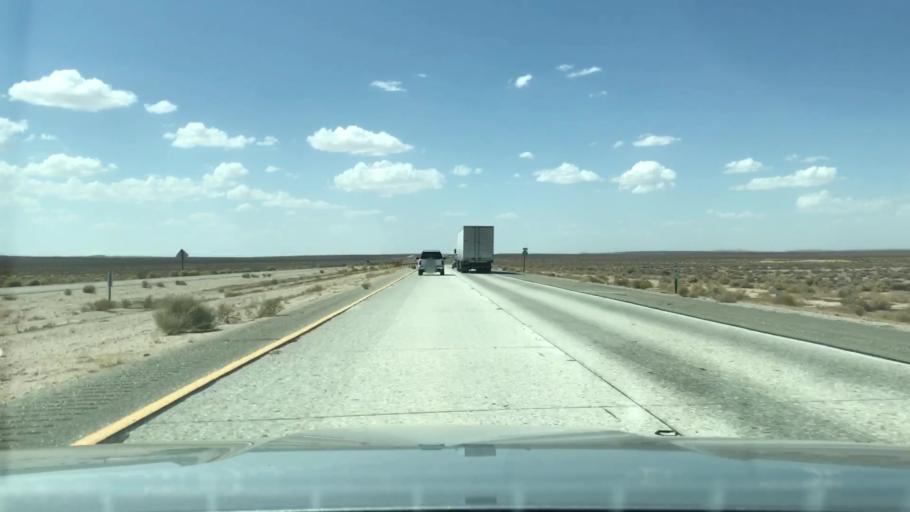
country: US
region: California
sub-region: San Bernardino County
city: Lenwood
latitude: 34.9335
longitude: -117.3684
